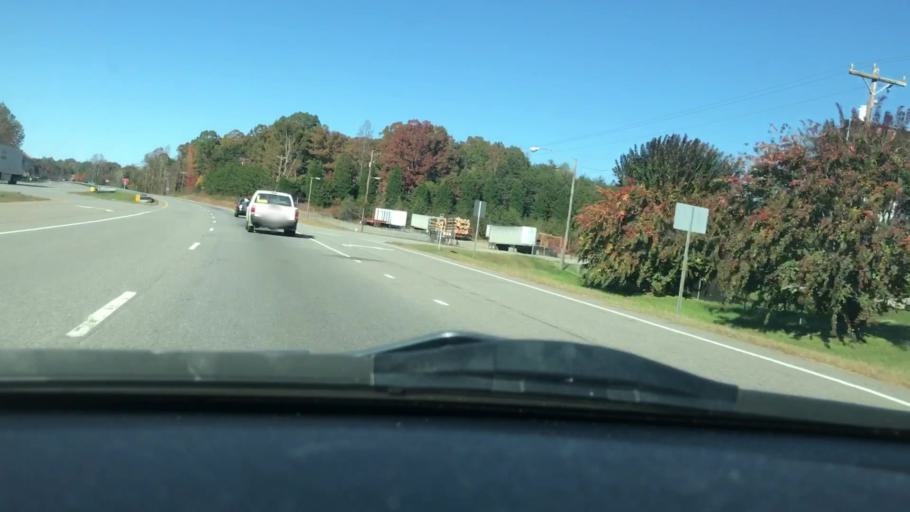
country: US
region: North Carolina
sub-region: Rockingham County
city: Stoneville
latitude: 36.4792
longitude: -79.9240
